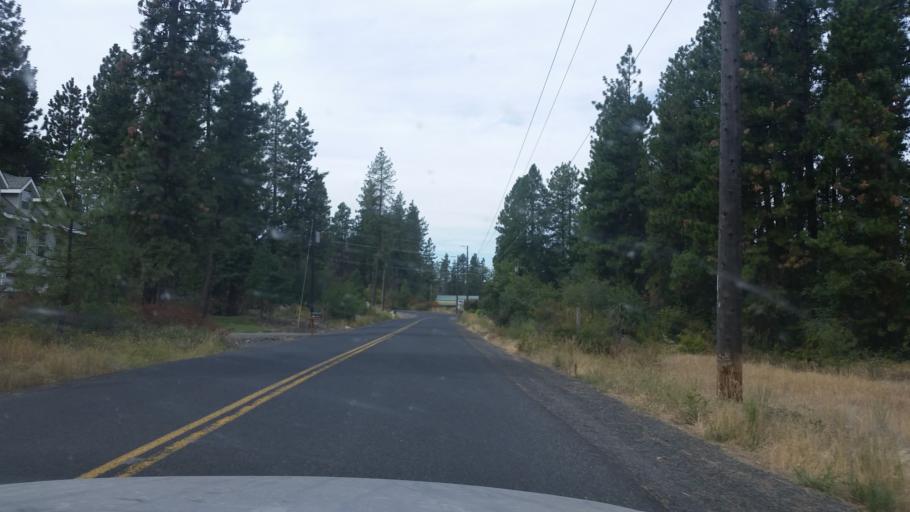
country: US
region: Washington
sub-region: Spokane County
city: Spokane
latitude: 47.6555
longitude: -117.4943
